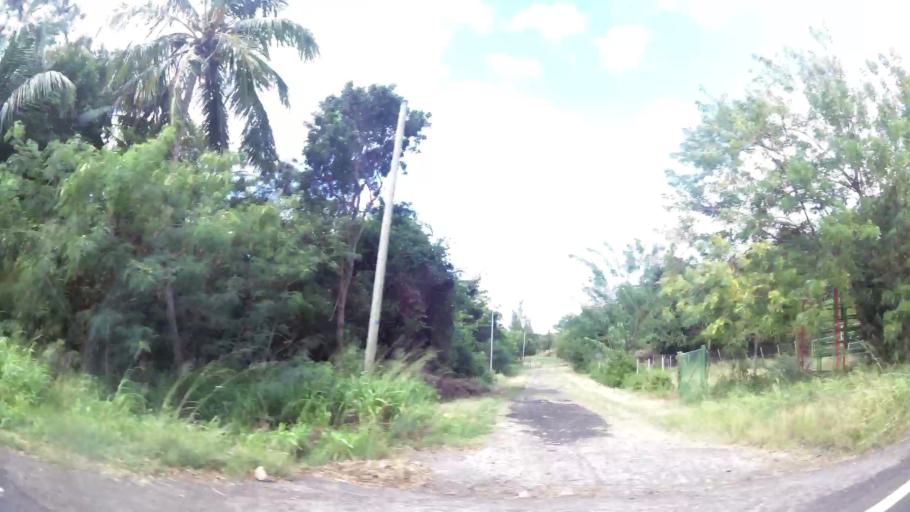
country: MQ
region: Martinique
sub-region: Martinique
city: Le Marin
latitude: 14.4584
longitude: -60.8603
